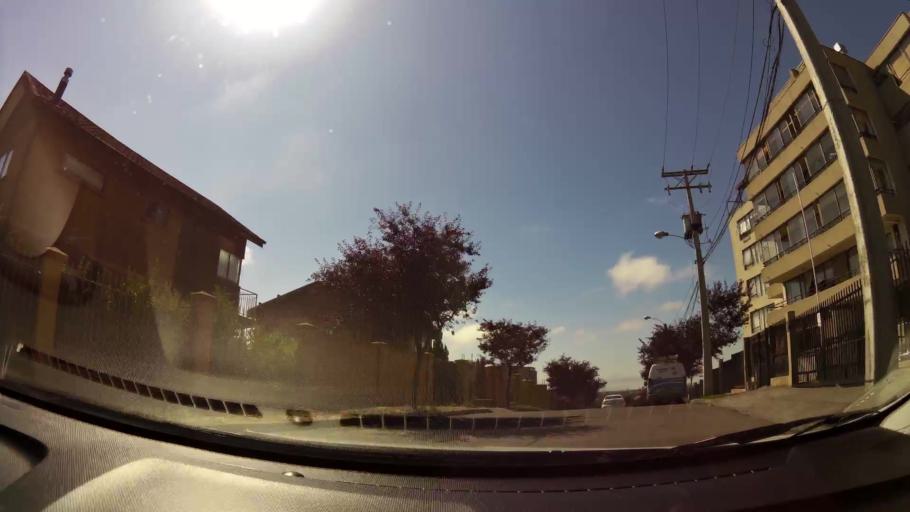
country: CL
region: Biobio
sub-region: Provincia de Concepcion
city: Concepcion
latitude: -36.7816
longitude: -73.0467
